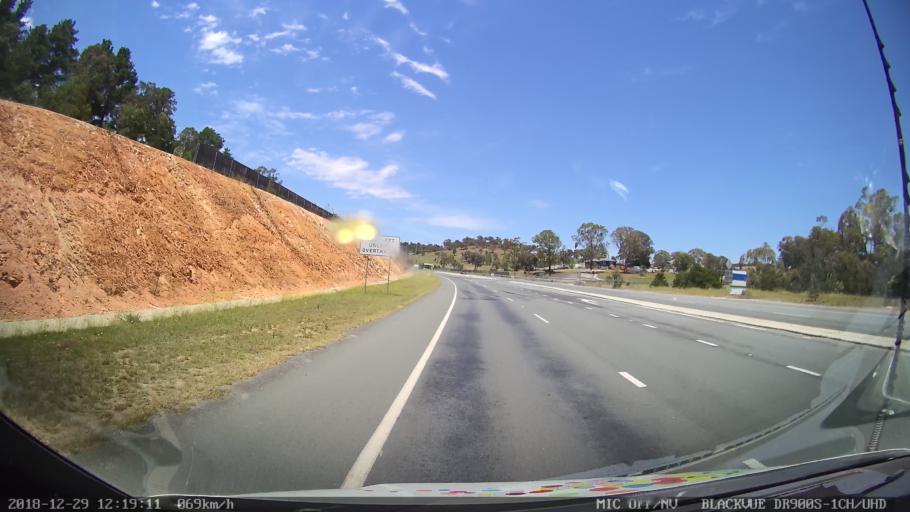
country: AU
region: New South Wales
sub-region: Queanbeyan
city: Queanbeyan
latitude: -35.3912
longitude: 149.2338
